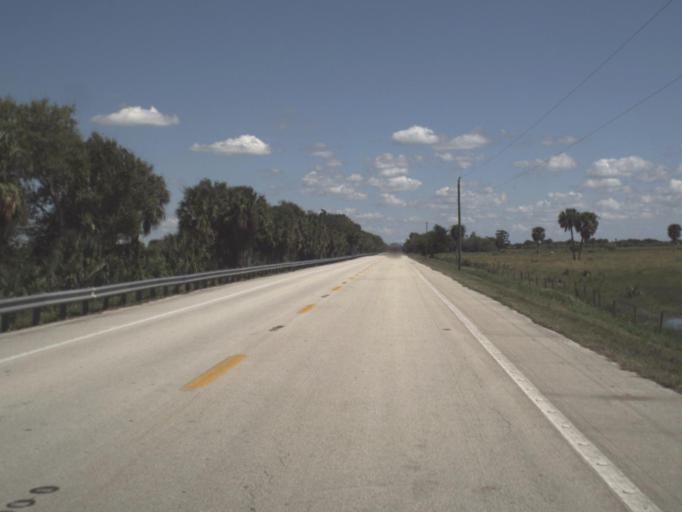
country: US
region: Florida
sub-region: Glades County
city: Buckhead Ridge
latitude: 27.1226
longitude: -80.9170
